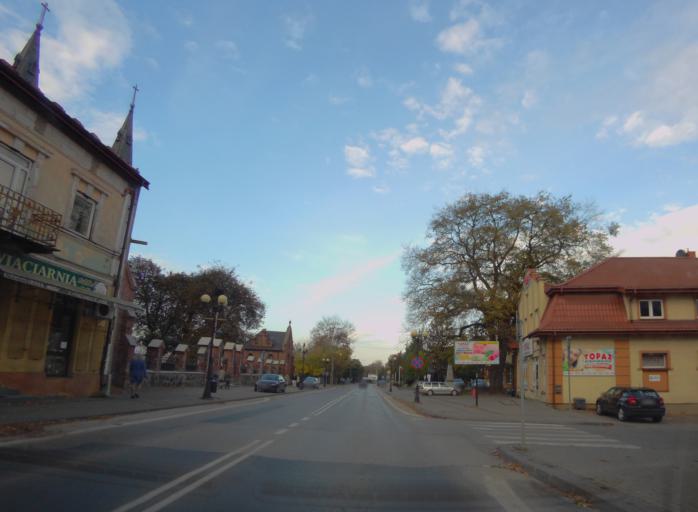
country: PL
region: Masovian Voivodeship
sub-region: Powiat losicki
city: Losice
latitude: 52.2116
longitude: 22.7160
